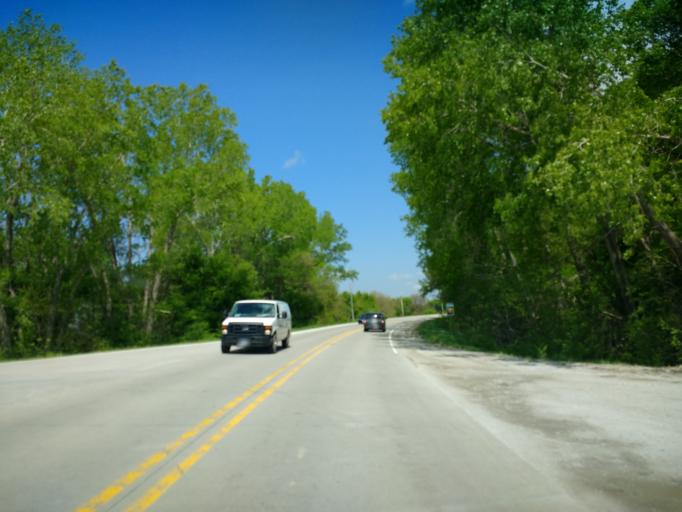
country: US
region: Iowa
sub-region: Harrison County
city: Missouri Valley
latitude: 41.4340
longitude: -95.8679
